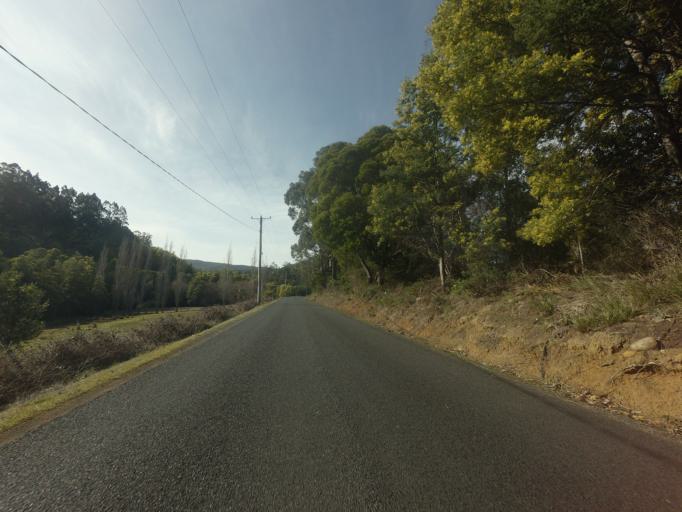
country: AU
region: Tasmania
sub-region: Huon Valley
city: Cygnet
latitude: -43.1783
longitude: 147.1459
